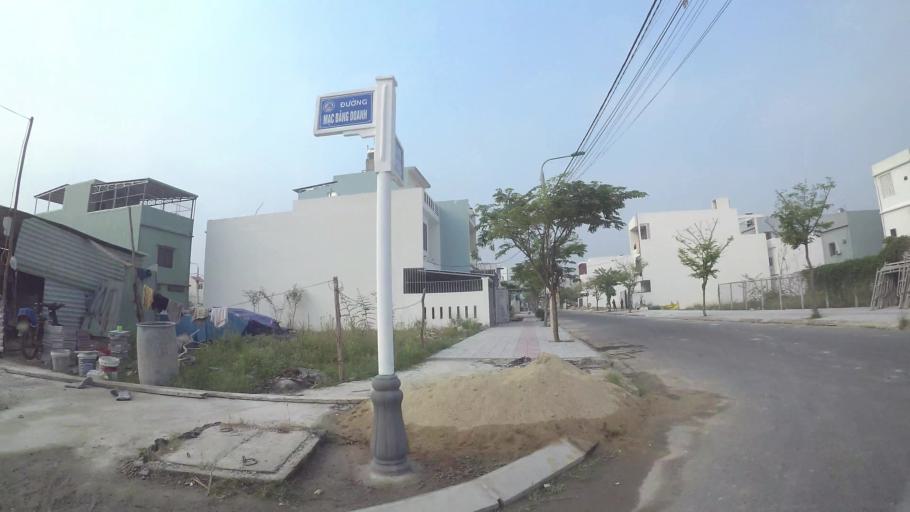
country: VN
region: Da Nang
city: Cam Le
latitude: 16.0163
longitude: 108.2199
